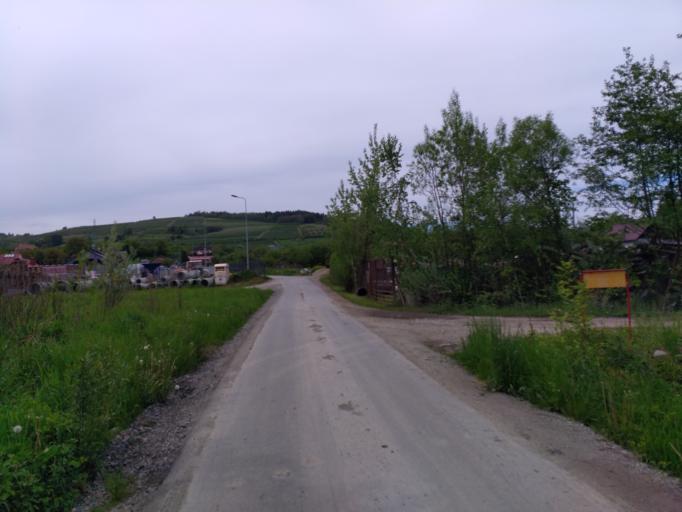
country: PL
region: Lesser Poland Voivodeship
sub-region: Powiat nowosadecki
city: Lacko
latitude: 49.5518
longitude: 20.4296
